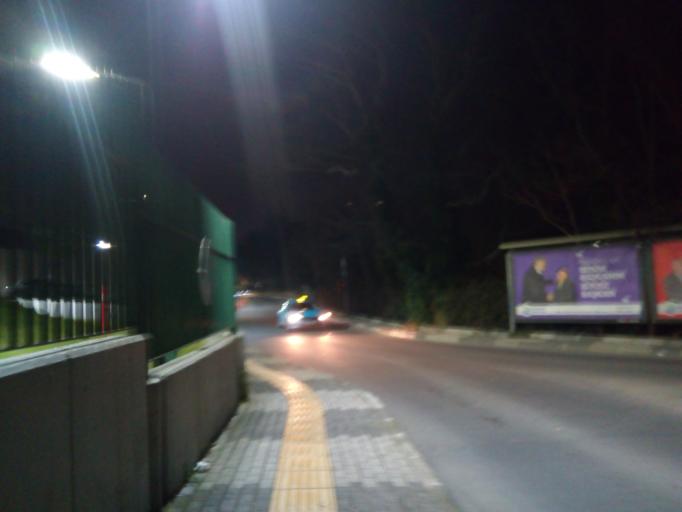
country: TR
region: Istanbul
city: Sisli
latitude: 41.1110
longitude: 29.0396
